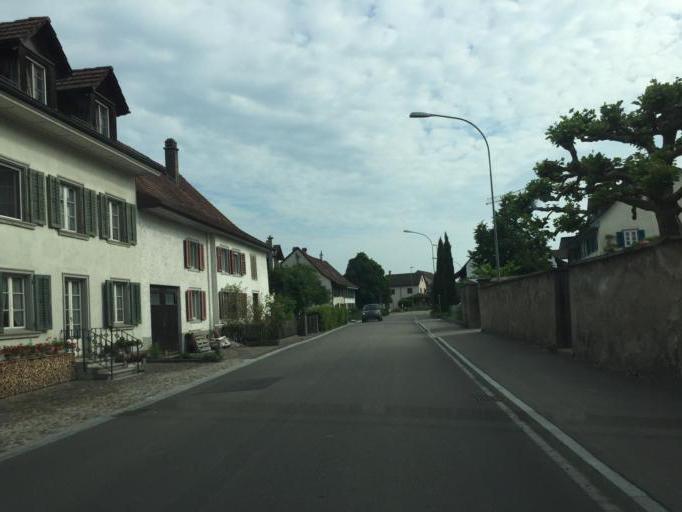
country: CH
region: Zurich
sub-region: Bezirk Andelfingen
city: Dachsen
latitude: 47.6418
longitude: 8.5999
